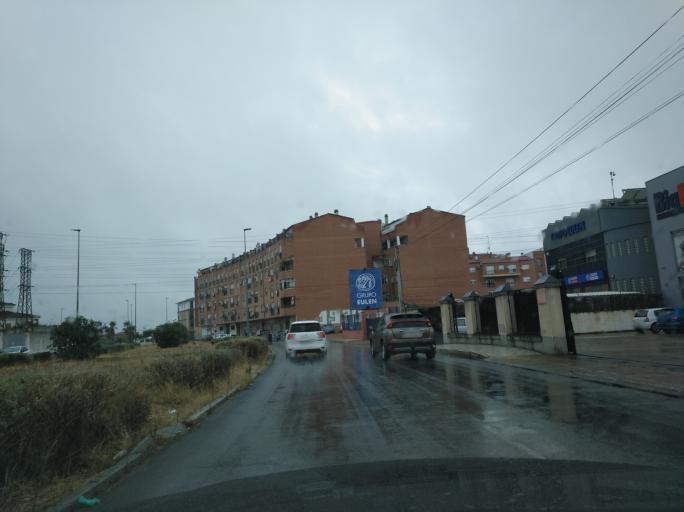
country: ES
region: Extremadura
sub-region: Provincia de Badajoz
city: Badajoz
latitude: 38.8896
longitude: -6.9930
